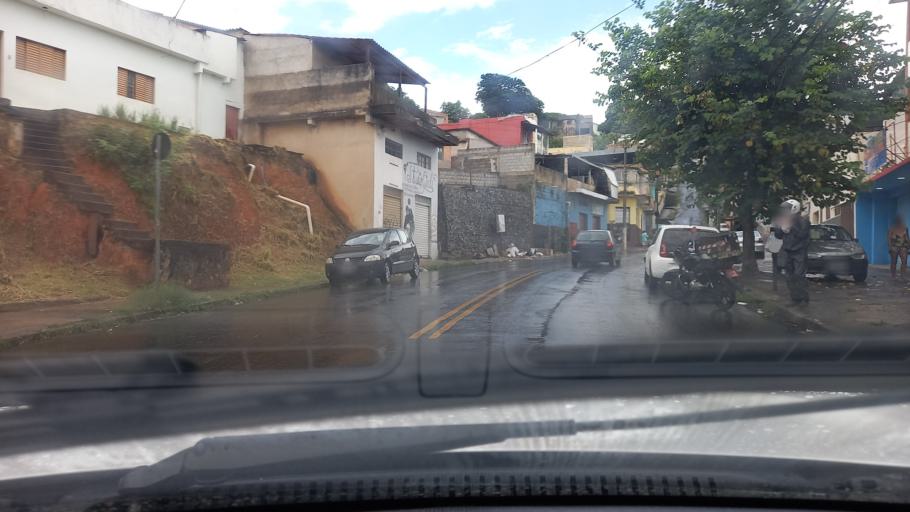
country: BR
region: Minas Gerais
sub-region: Belo Horizonte
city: Belo Horizonte
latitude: -19.9051
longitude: -43.9482
